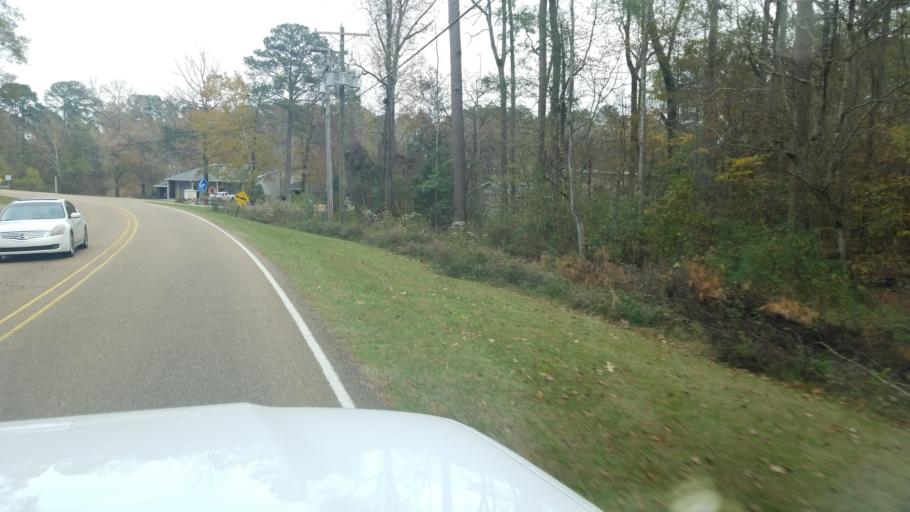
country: US
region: Mississippi
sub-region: Rankin County
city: Brandon
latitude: 32.3718
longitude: -90.0142
